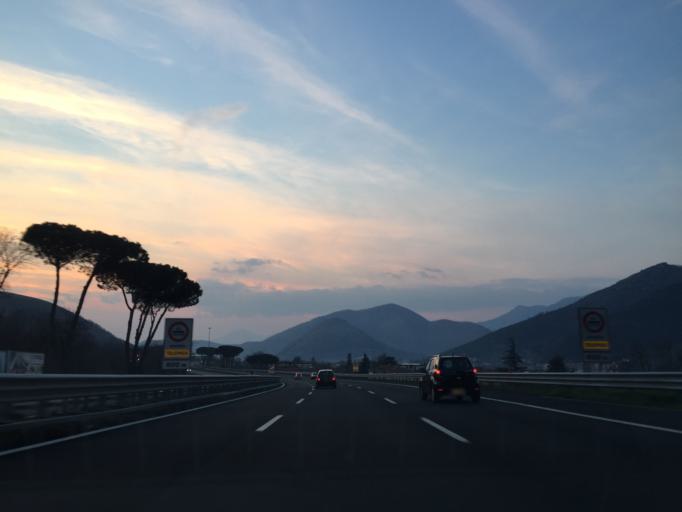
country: IT
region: Campania
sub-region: Provincia di Salerno
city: Piazza del Galdo-Sant'Angelo
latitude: 40.7719
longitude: 14.7351
